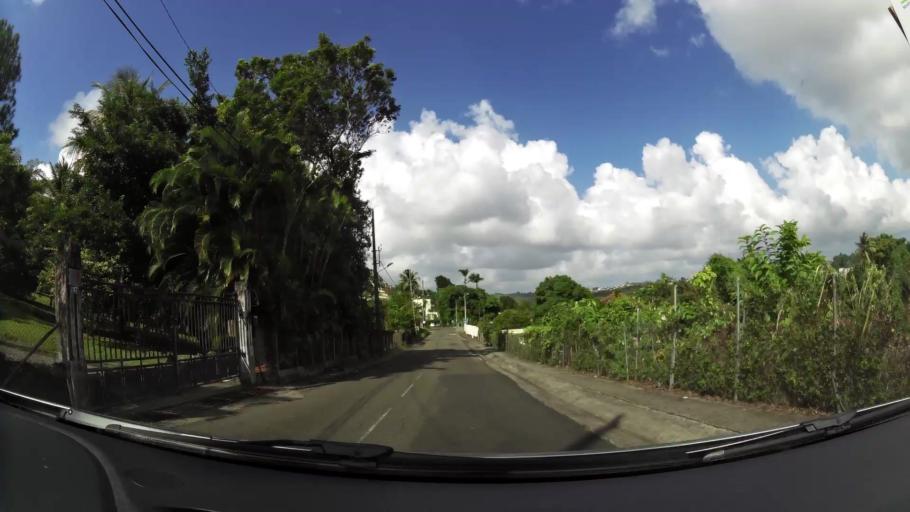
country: MQ
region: Martinique
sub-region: Martinique
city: Fort-de-France
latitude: 14.6287
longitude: -61.0489
